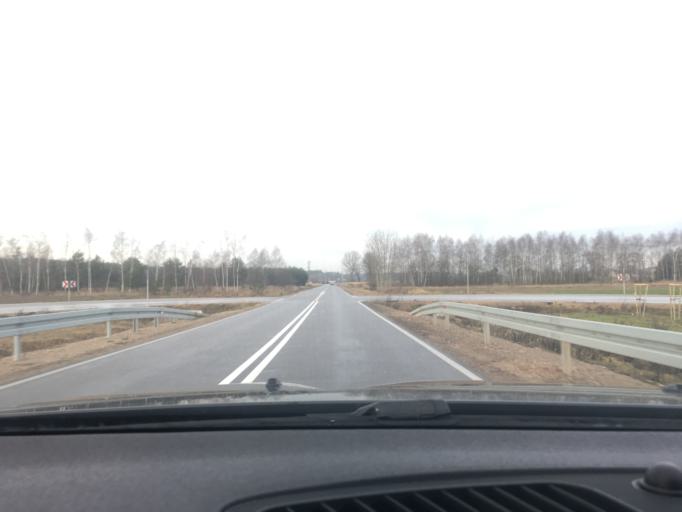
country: PL
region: Swietokrzyskie
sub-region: Powiat jedrzejowski
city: Jedrzejow
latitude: 50.6926
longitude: 20.3672
